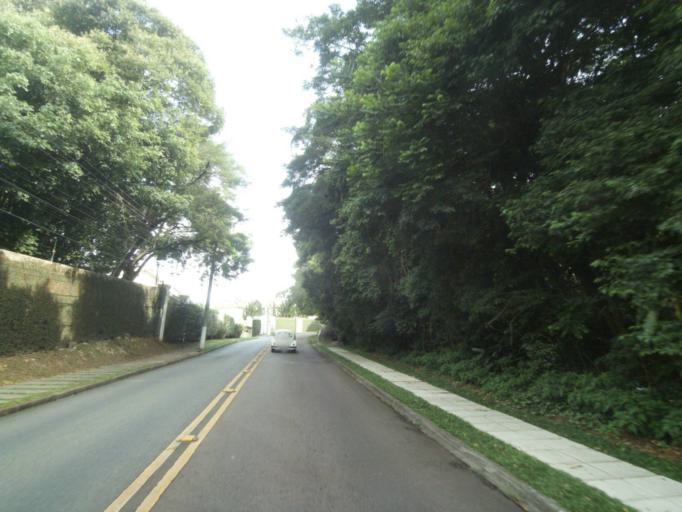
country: BR
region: Parana
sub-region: Curitiba
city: Curitiba
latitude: -25.4062
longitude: -49.2986
